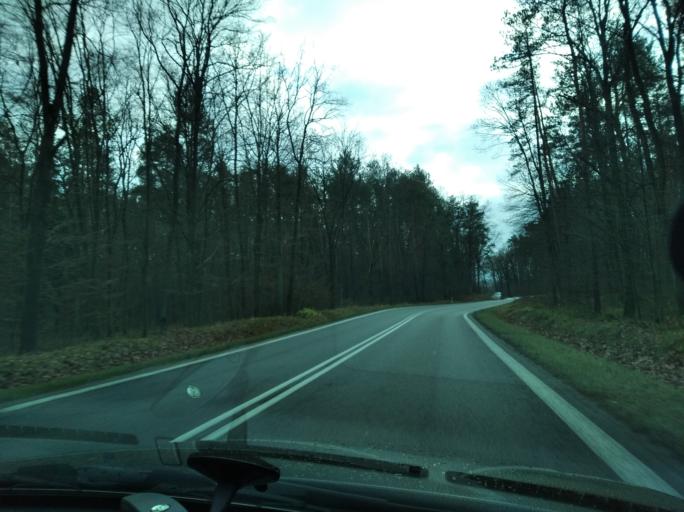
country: PL
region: Subcarpathian Voivodeship
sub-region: Powiat lancucki
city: Rakszawa
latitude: 50.1284
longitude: 22.2319
